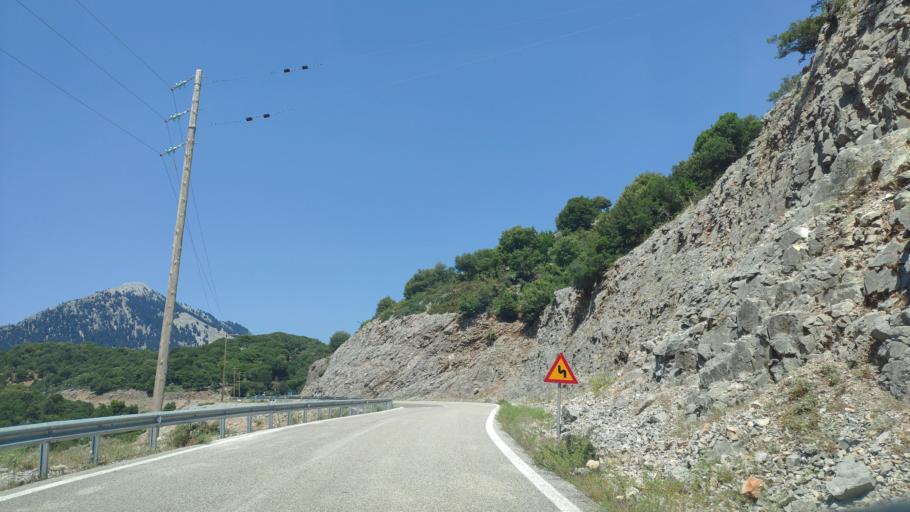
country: GR
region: Central Greece
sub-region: Nomos Evrytanias
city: Kerasochori
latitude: 38.9679
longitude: 21.4669
